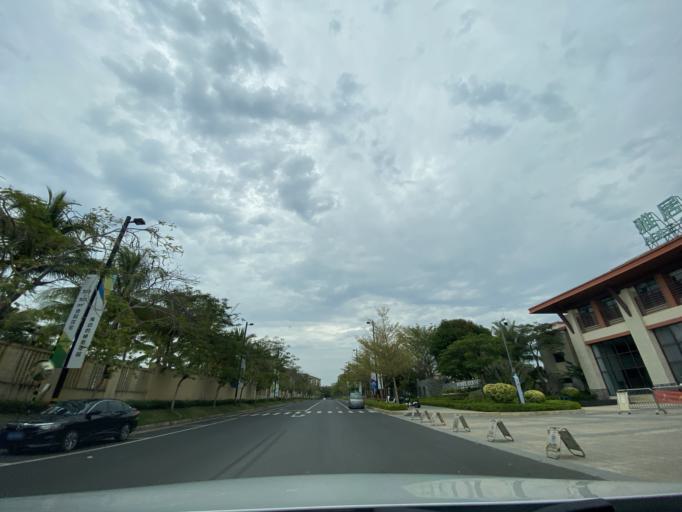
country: CN
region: Hainan
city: Yingzhou
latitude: 18.4041
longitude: 109.8556
